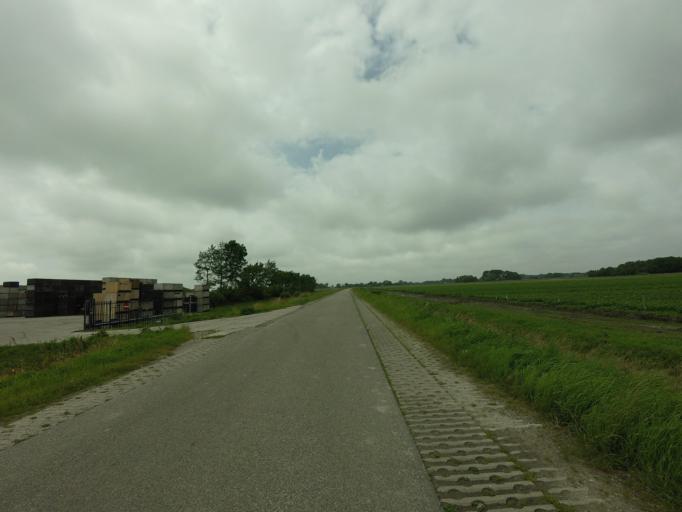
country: NL
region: North Holland
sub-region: Gemeente Schagen
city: Schagen
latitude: 52.7700
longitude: 4.7851
